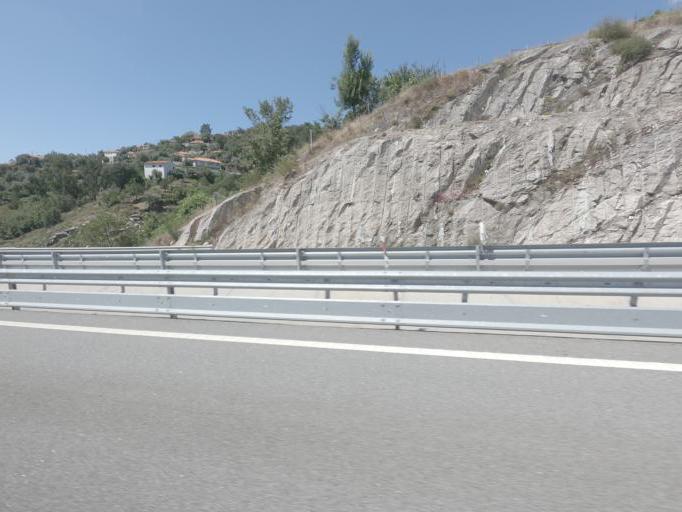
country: PT
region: Porto
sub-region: Baiao
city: Valadares
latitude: 41.2514
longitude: -7.9644
